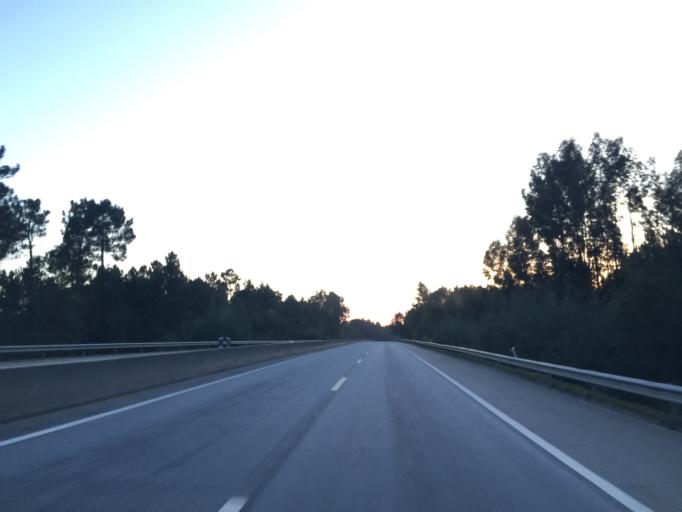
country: PT
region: Viseu
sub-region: Concelho de Carregal do Sal
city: Carregal do Sal
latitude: 40.4221
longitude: -8.0299
